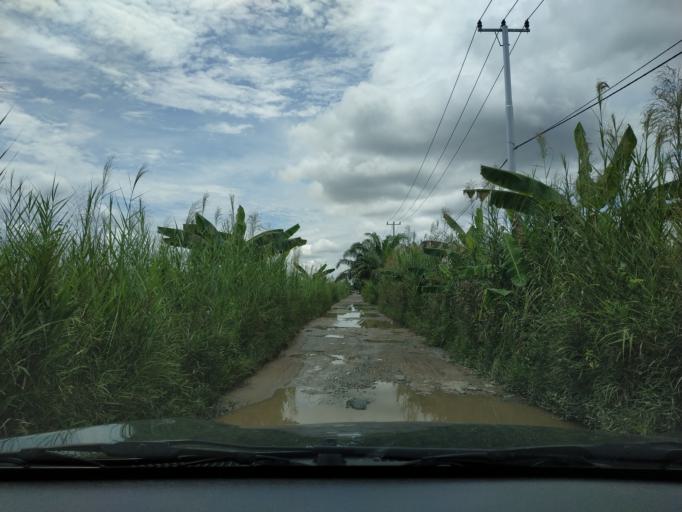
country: ID
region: Riau
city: Tembilahan
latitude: -0.3111
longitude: 103.1770
